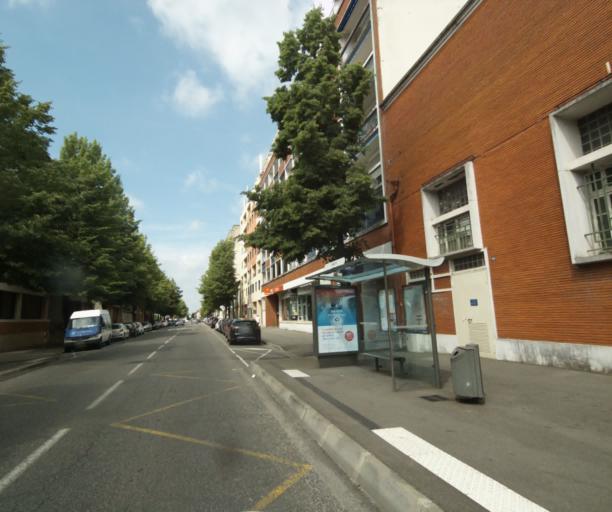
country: FR
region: Midi-Pyrenees
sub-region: Departement du Tarn-et-Garonne
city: Montauban
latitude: 44.0199
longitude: 1.3601
